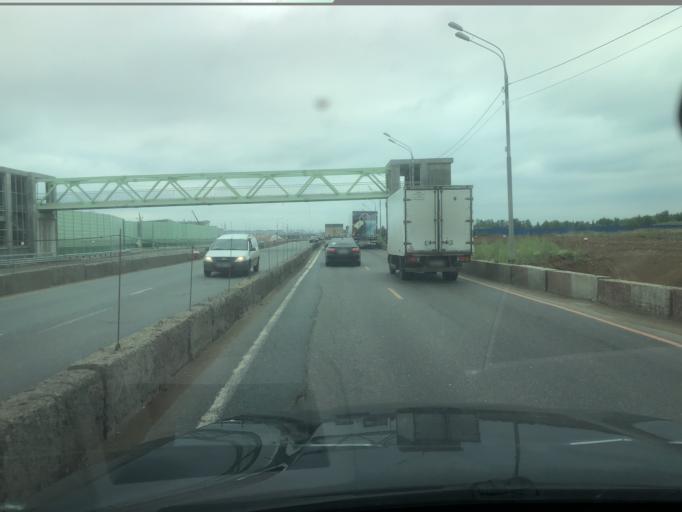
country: RU
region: Moskovskaya
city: Sheremet'yevskiy
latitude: 55.9999
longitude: 37.5375
